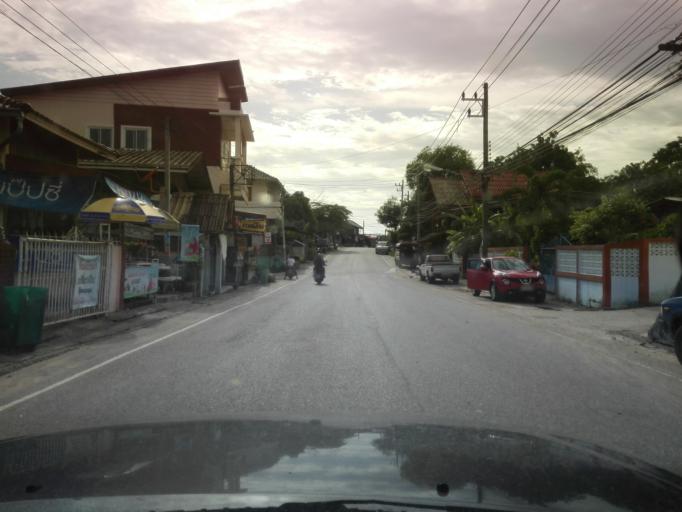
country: TH
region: Tak
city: Mae Ramat
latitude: 16.9798
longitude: 98.5224
